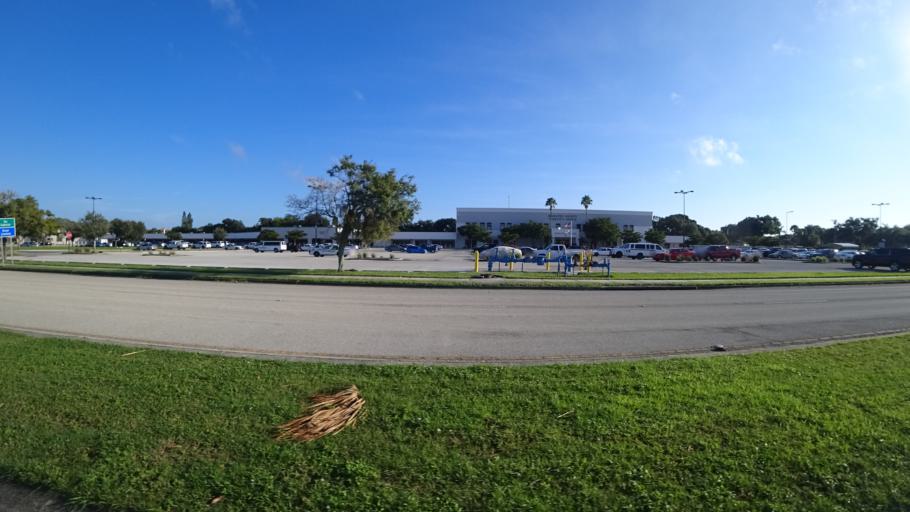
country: US
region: Florida
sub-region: Manatee County
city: West Samoset
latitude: 27.4690
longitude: -82.5679
